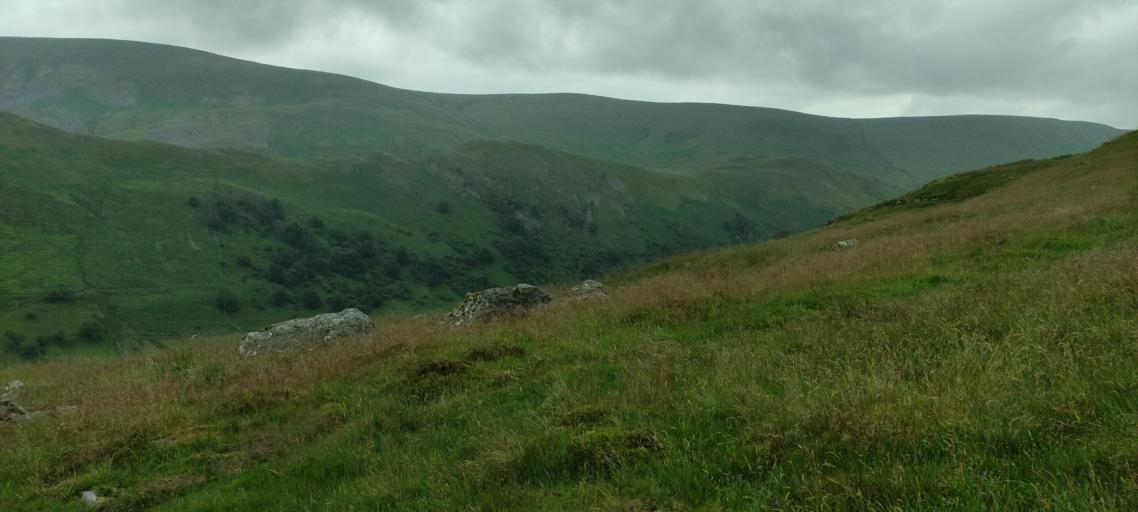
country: GB
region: England
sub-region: Cumbria
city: Ambleside
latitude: 54.5517
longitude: -2.8846
